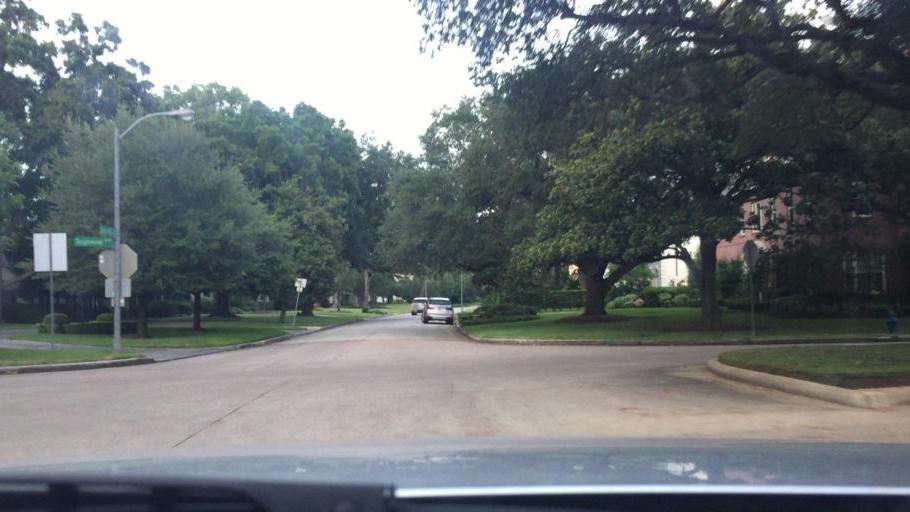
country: US
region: Texas
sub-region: Harris County
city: Hunters Creek Village
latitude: 29.7581
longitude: -95.4734
